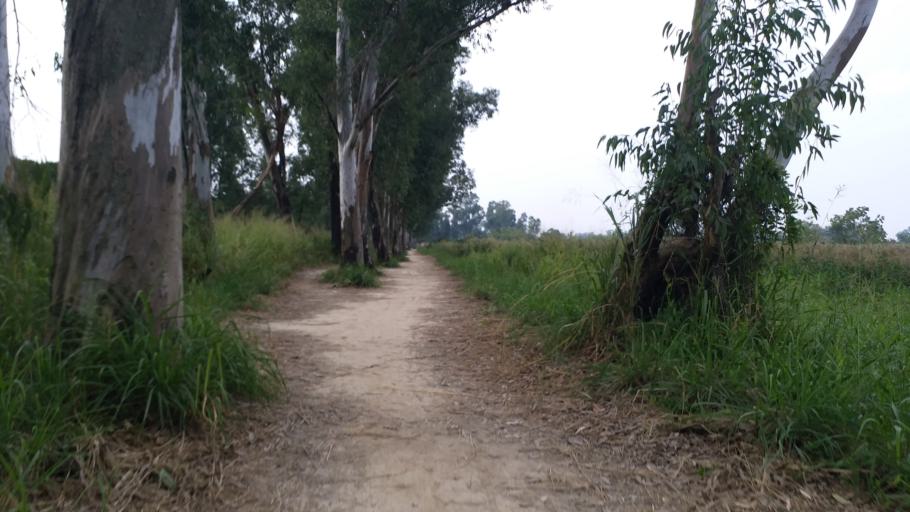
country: HK
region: Yuen Long
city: Yuen Long Kau Hui
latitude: 22.4560
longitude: 114.0347
